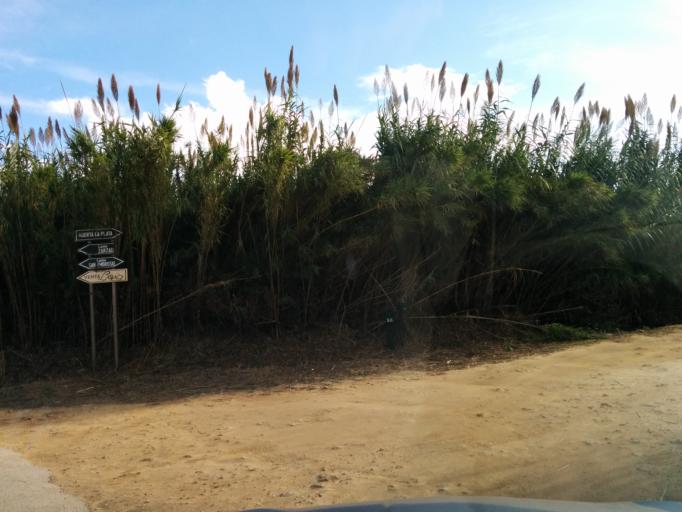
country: ES
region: Andalusia
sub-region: Provincia de Cadiz
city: Vejer de la Frontera
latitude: 36.2109
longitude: -5.9995
